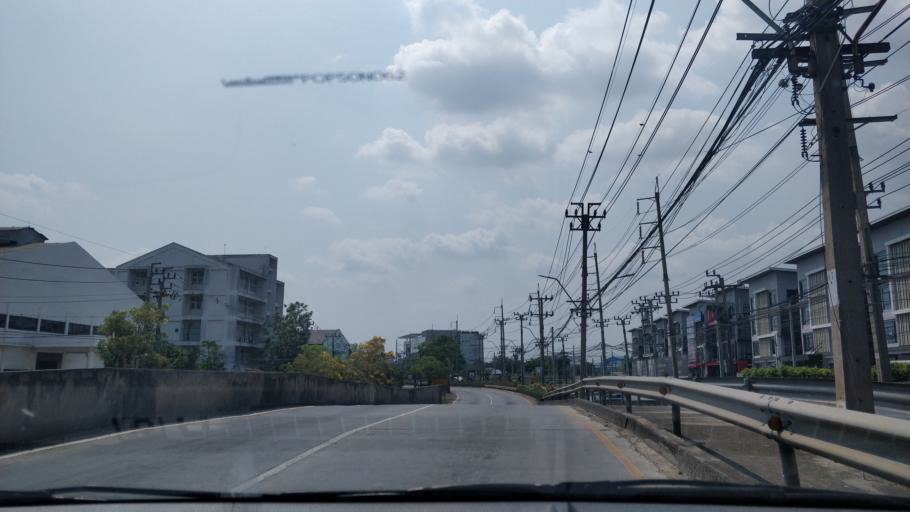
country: TH
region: Bangkok
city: Lat Krabang
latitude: 13.7574
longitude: 100.7930
